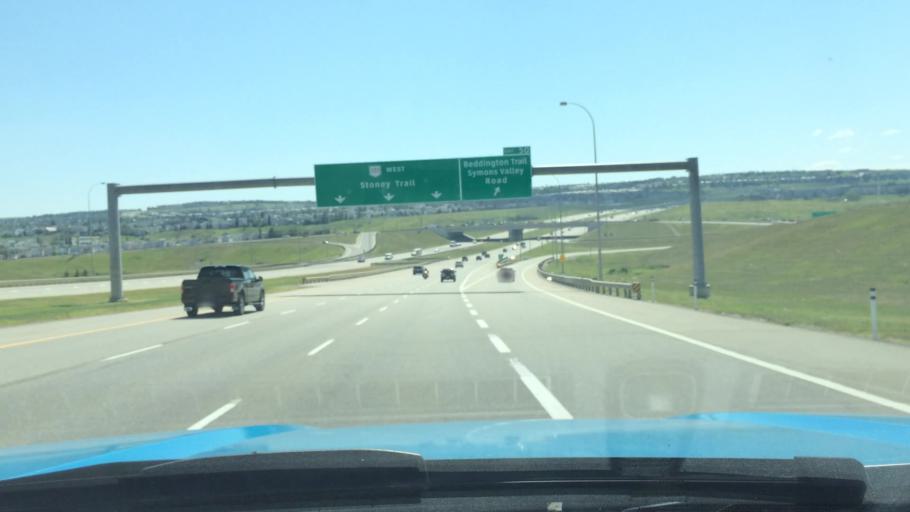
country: CA
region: Alberta
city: Calgary
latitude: 51.1610
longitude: -114.1105
